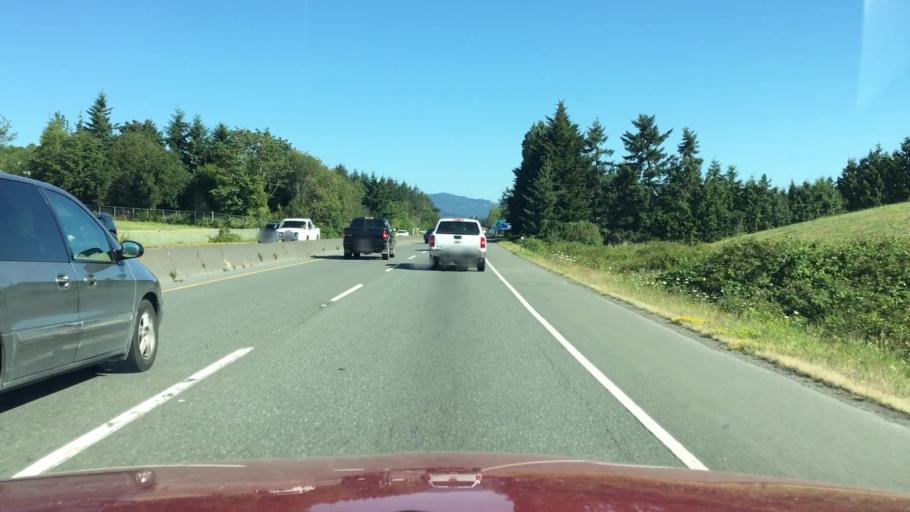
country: CA
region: British Columbia
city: North Saanich
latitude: 48.6217
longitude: -123.4084
